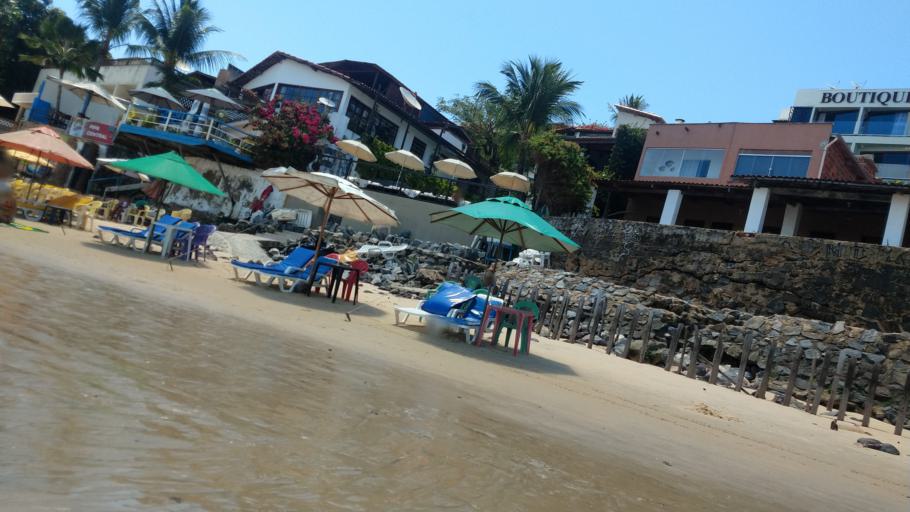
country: BR
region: Rio Grande do Norte
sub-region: Ares
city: Ares
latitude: -6.2278
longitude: -35.0494
